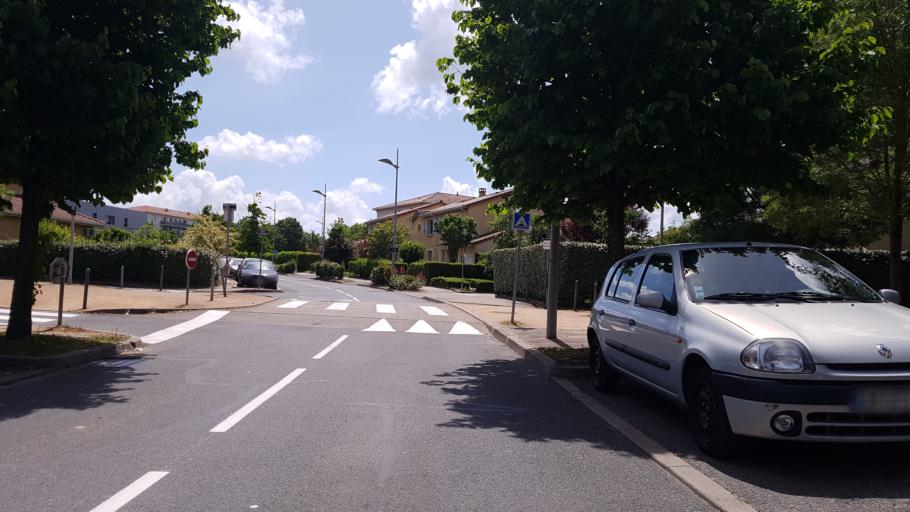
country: FR
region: Rhone-Alpes
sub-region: Departement du Rhone
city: Rillieux-la-Pape
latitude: 45.8188
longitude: 4.8864
